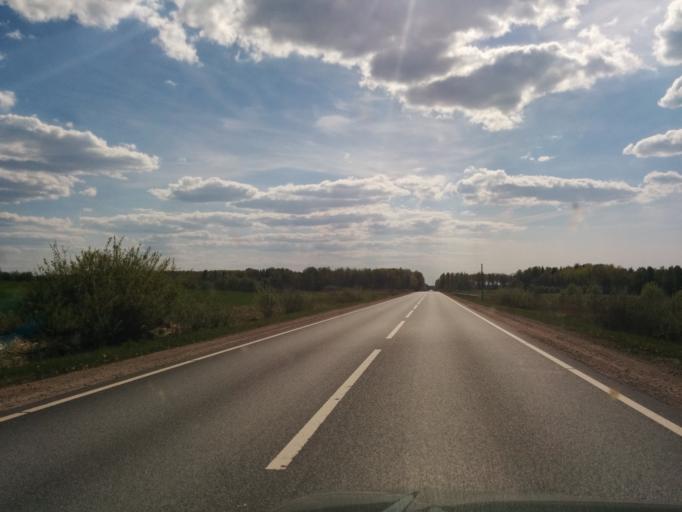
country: LV
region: Sigulda
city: Sigulda
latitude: 57.2391
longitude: 24.8293
